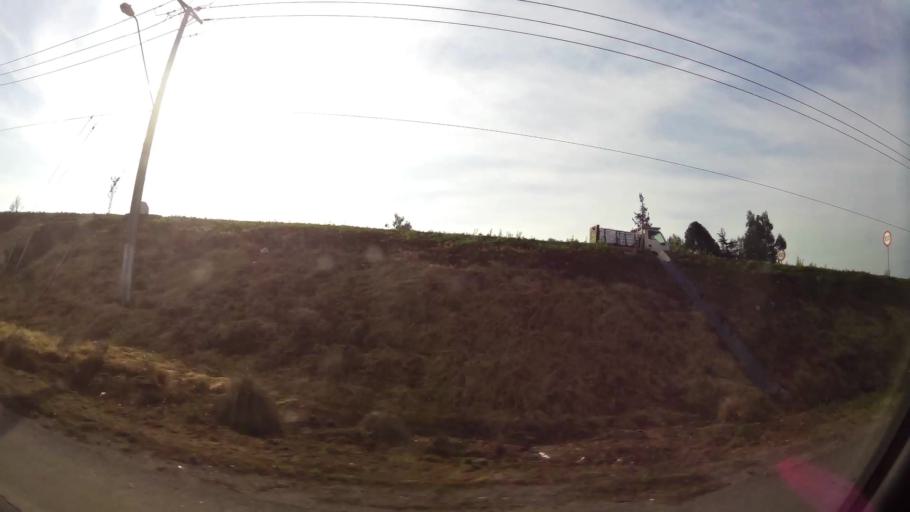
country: CL
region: Santiago Metropolitan
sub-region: Provincia de Talagante
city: Penaflor
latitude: -33.5969
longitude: -70.8450
